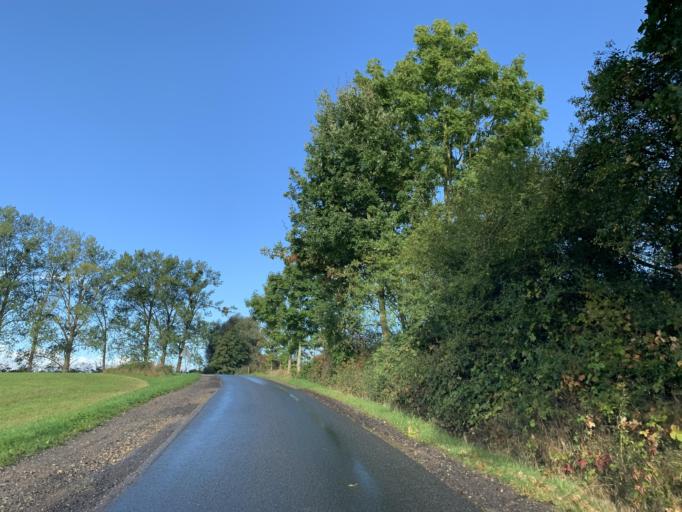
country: DE
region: Mecklenburg-Vorpommern
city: Burg Stargard
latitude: 53.4575
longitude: 13.2814
